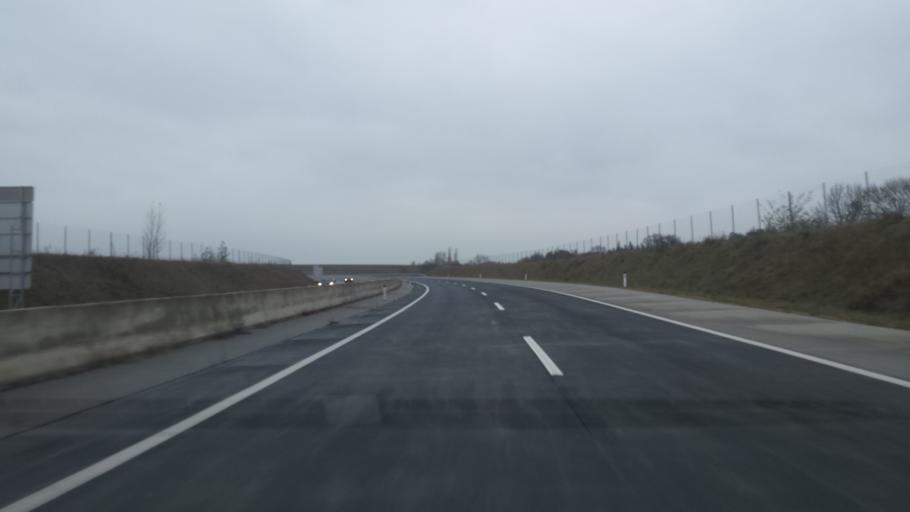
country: AT
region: Lower Austria
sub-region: Politischer Bezirk Mistelbach
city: Hochleithen
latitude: 48.4380
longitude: 16.5555
